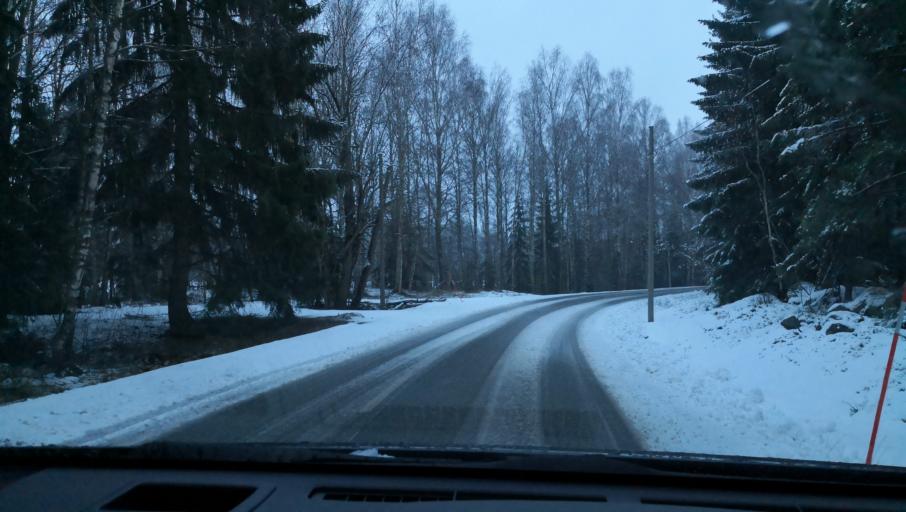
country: SE
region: Vaestmanland
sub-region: Kopings Kommun
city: Kolsva
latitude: 59.5823
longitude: 15.8037
